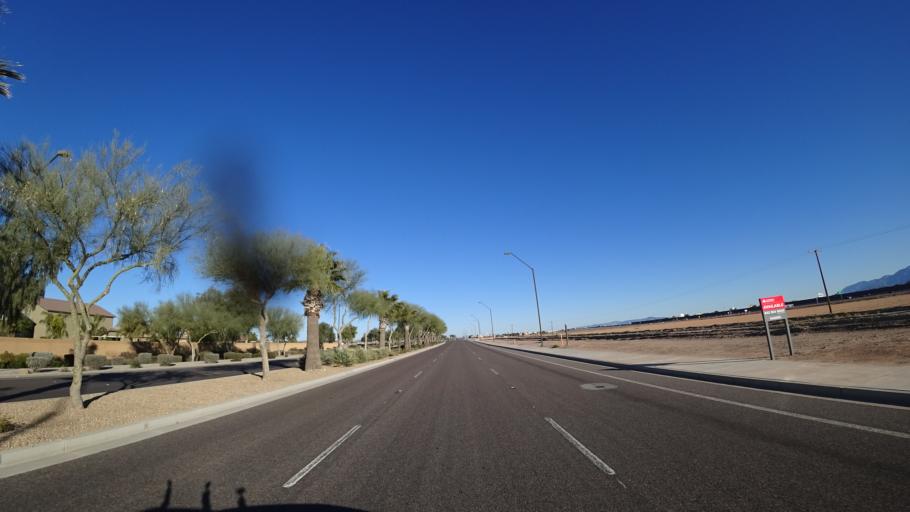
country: US
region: Arizona
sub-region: Maricopa County
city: Litchfield Park
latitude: 33.4648
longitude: -112.4044
